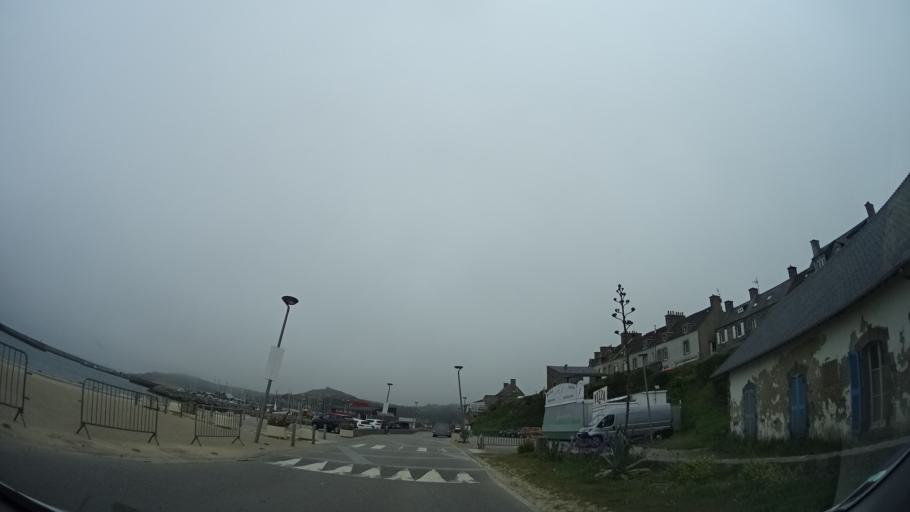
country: FR
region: Lower Normandy
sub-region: Departement de la Manche
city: Flamanville
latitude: 49.5502
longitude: -1.8635
